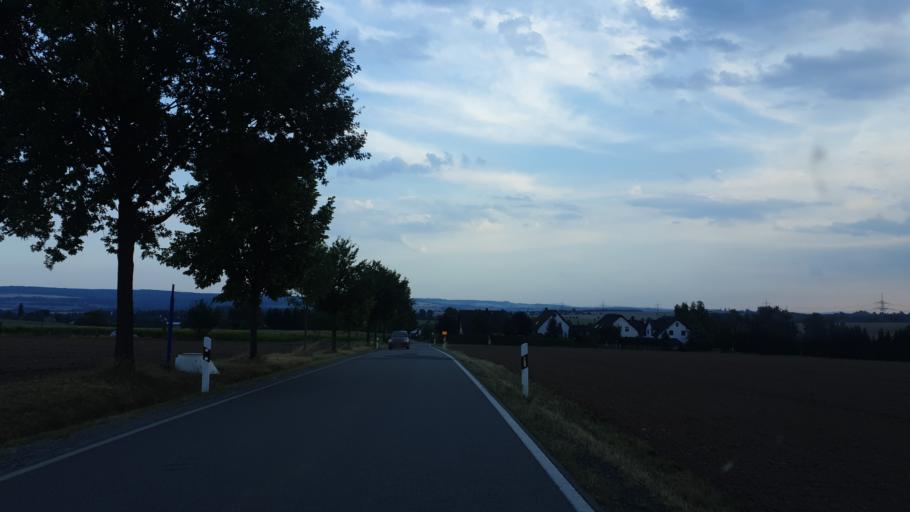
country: DE
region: Saxony
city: Niederdorf
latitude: 50.7833
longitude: 12.8050
